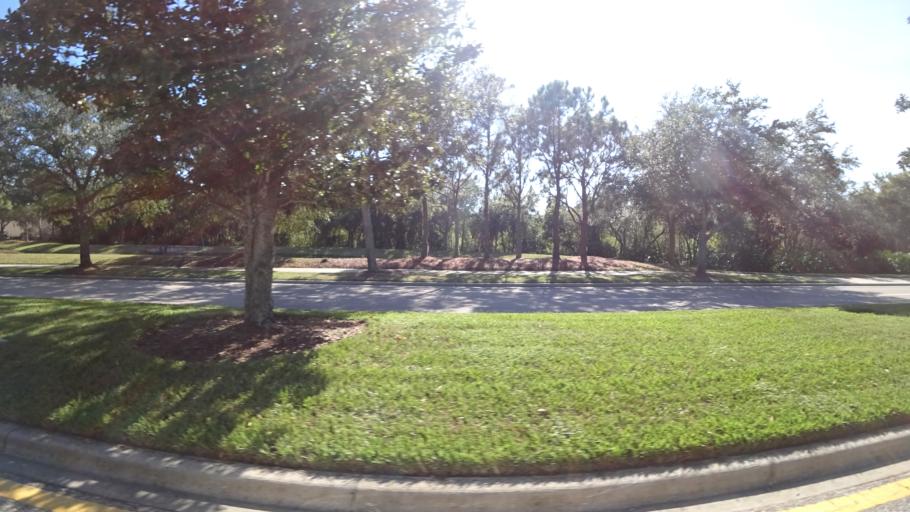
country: US
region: Florida
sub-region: Sarasota County
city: The Meadows
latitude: 27.3915
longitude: -82.4445
